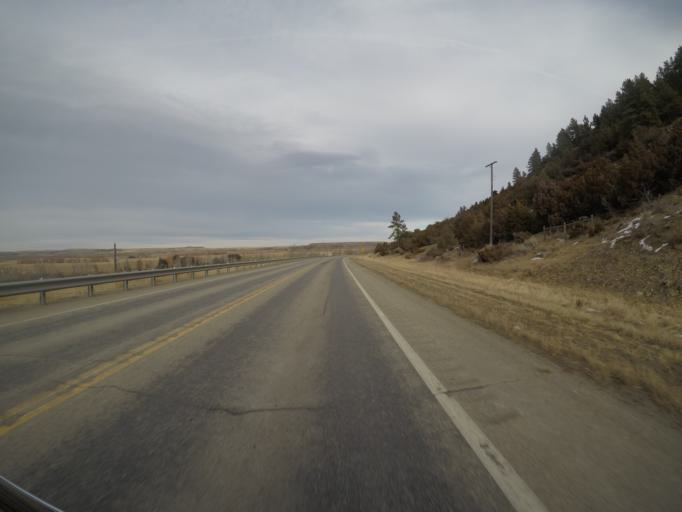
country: US
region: Montana
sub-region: Stillwater County
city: Absarokee
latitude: 45.5311
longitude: -109.4277
